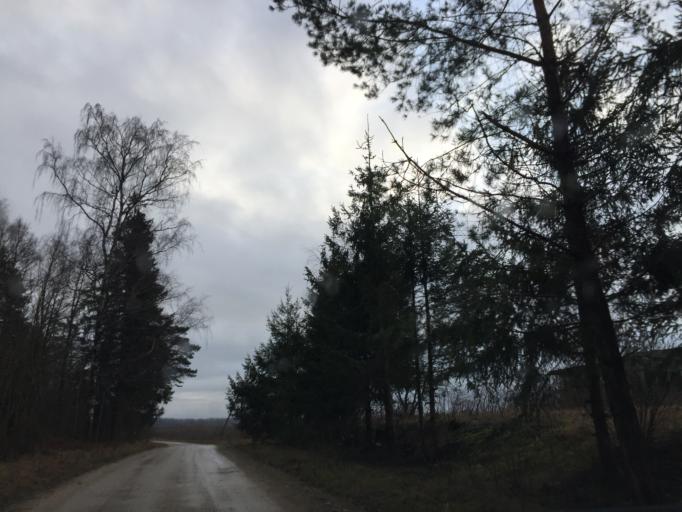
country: LV
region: Vainode
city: Vainode
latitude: 56.6060
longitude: 21.7996
